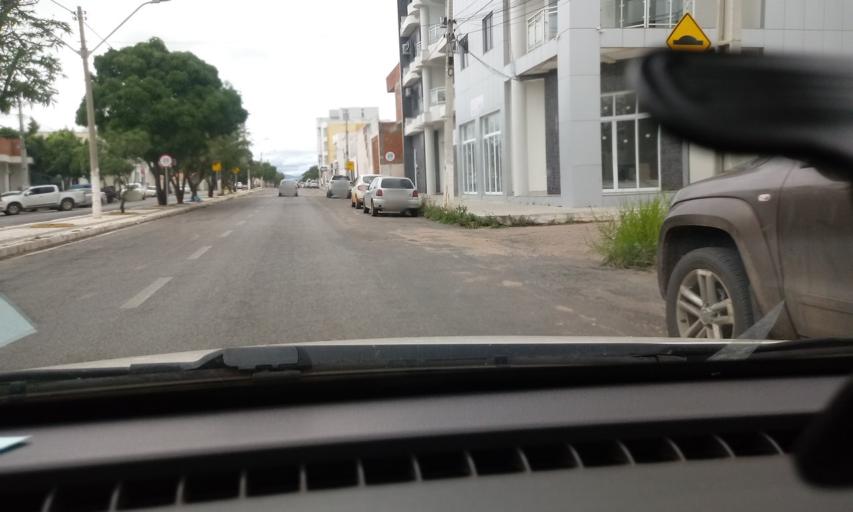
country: BR
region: Bahia
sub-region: Guanambi
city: Guanambi
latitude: -14.2145
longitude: -42.7867
